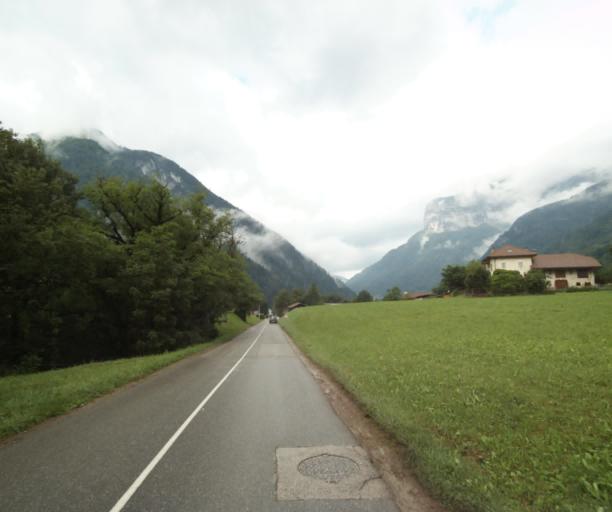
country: FR
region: Rhone-Alpes
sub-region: Departement de la Haute-Savoie
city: Thones
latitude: 45.8964
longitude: 6.3053
